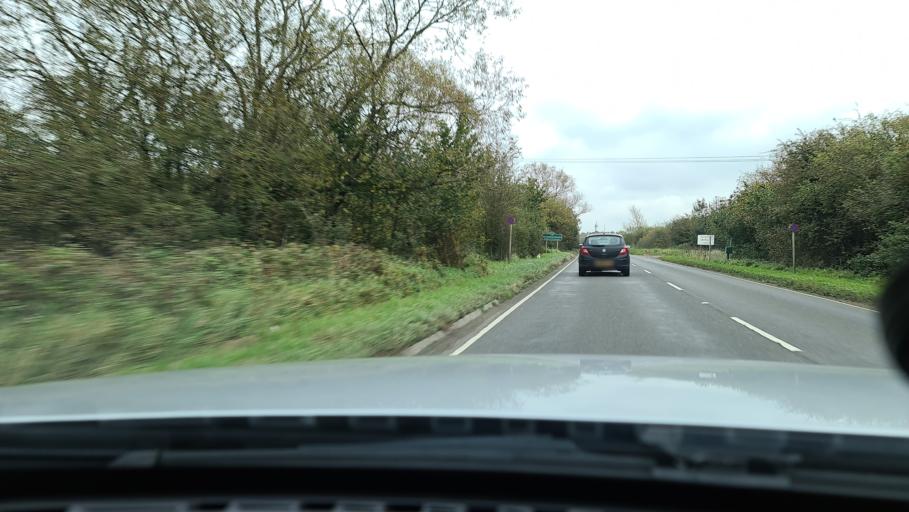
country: GB
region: England
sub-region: Oxfordshire
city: Bicester
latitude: 51.8742
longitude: -1.0697
